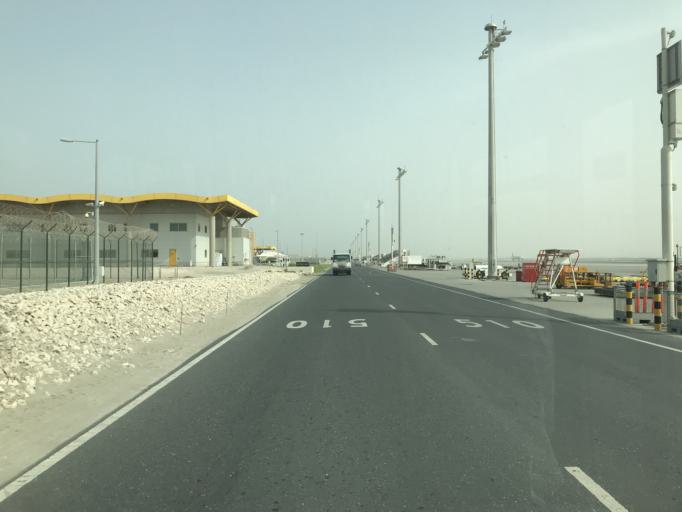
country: QA
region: Baladiyat ad Dawhah
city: Doha
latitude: 25.2787
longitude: 51.5990
